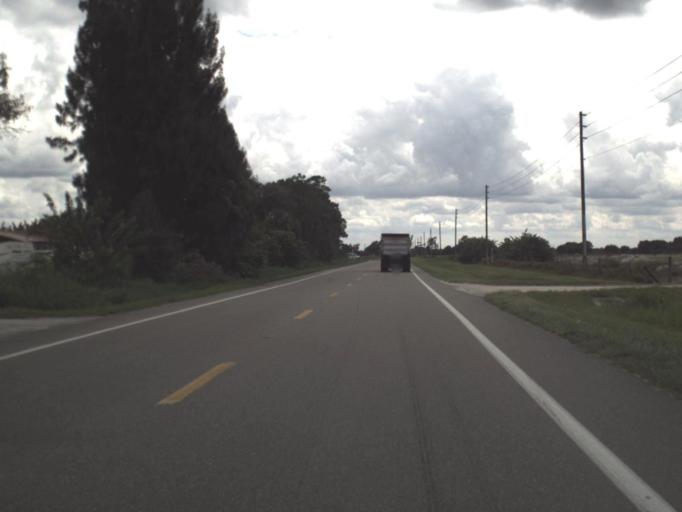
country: US
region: Florida
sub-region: DeSoto County
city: Nocatee
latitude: 26.9975
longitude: -81.7605
